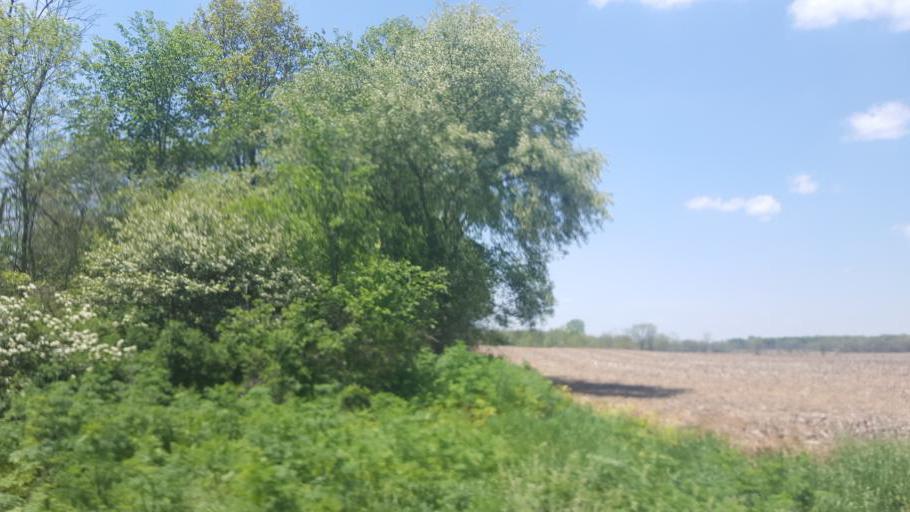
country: US
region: Ohio
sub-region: Knox County
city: Oak Hill
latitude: 40.2924
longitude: -82.2837
